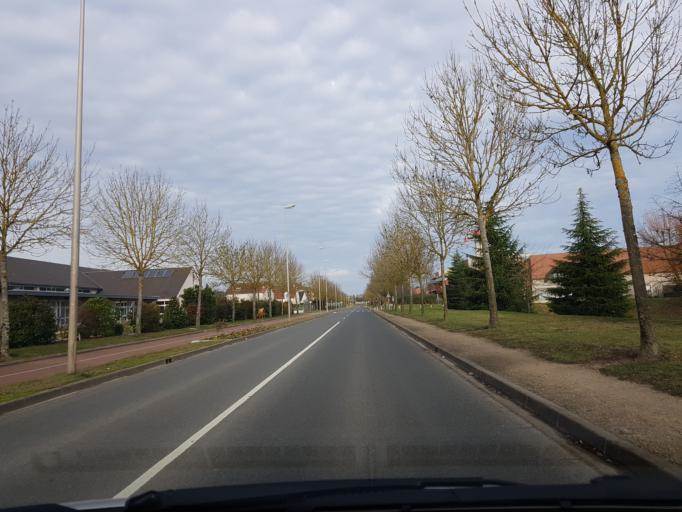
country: FR
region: Centre
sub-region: Departement du Loiret
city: Saint-Jean-le-Blanc
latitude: 47.8883
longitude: 1.9292
